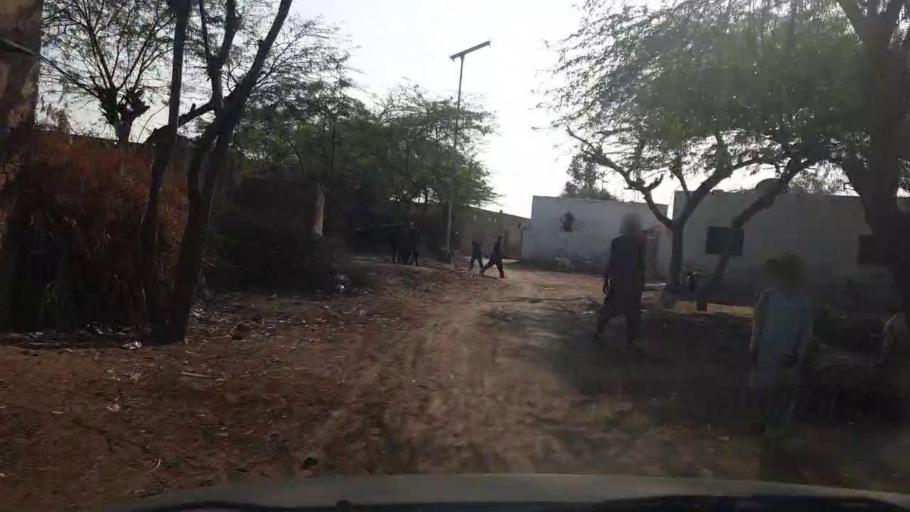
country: PK
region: Sindh
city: Digri
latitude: 25.2530
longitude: 69.1786
